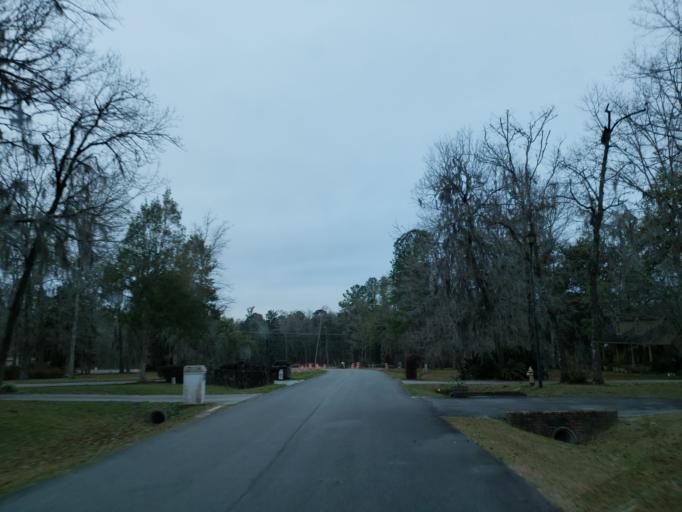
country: US
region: Georgia
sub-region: Lowndes County
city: Remerton
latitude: 30.8954
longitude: -83.3639
